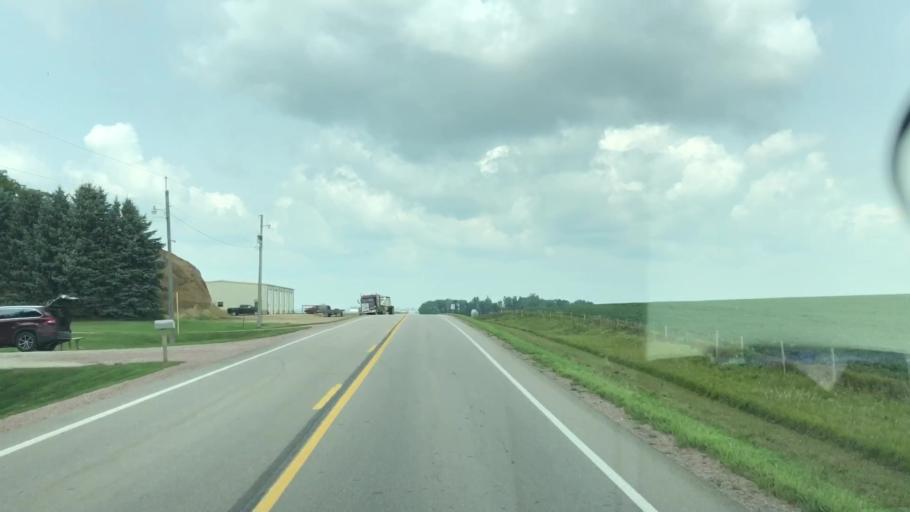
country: US
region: Iowa
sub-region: Plymouth County
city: Kingsley
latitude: 42.5920
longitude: -95.9574
